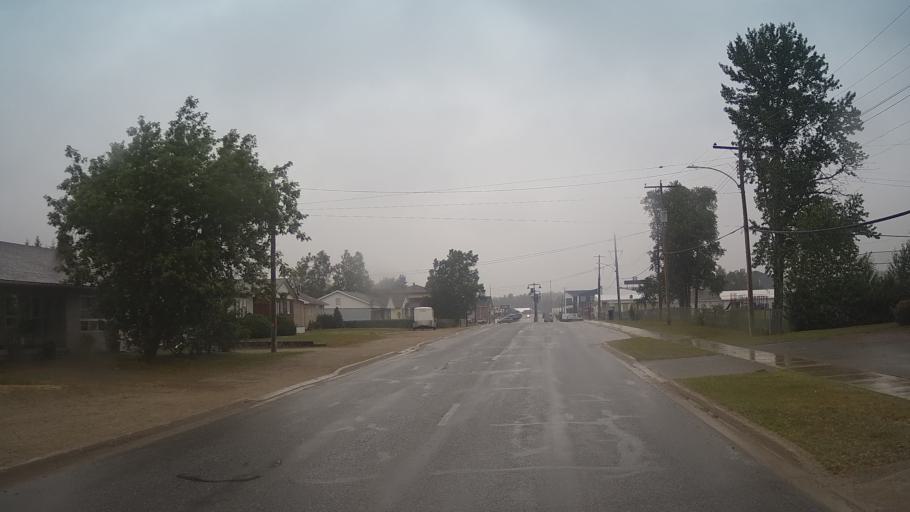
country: CA
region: Ontario
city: Greenstone
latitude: 49.7782
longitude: -86.5355
